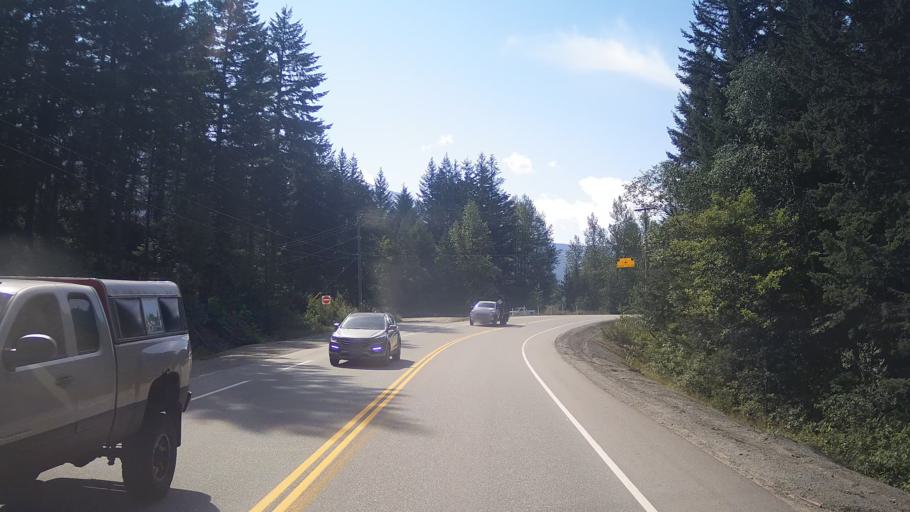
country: CA
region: British Columbia
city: Whistler
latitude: 50.2137
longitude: -122.8841
